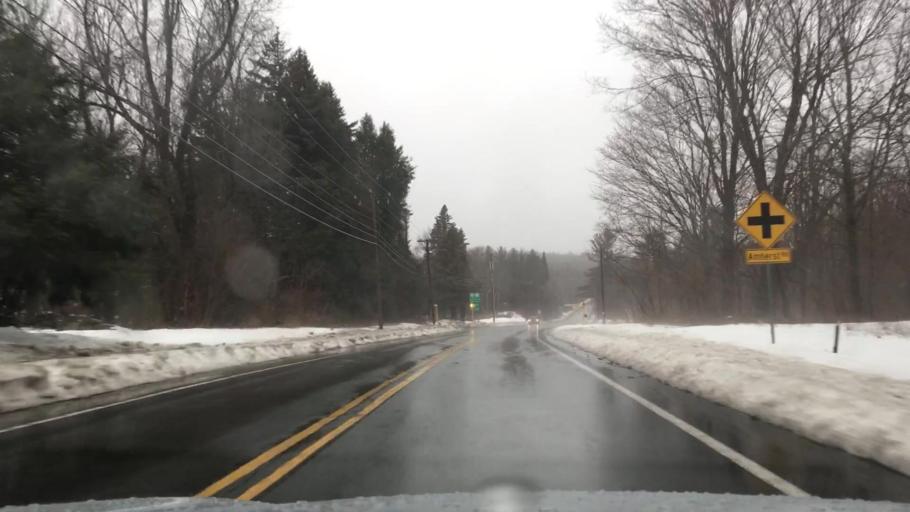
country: US
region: Massachusetts
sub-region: Hampshire County
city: Pelham
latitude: 42.3913
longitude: -72.4032
